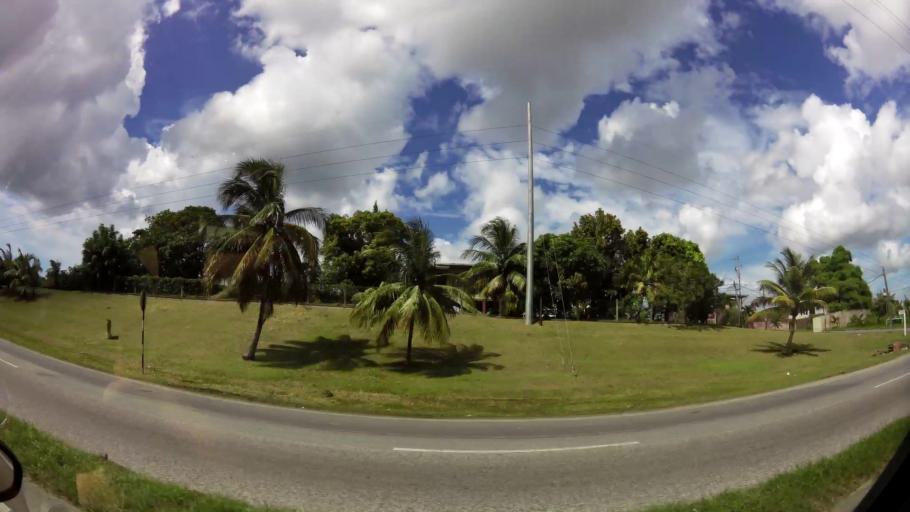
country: TT
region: City of San Fernando
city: San Fernando
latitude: 10.2590
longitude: -61.4653
